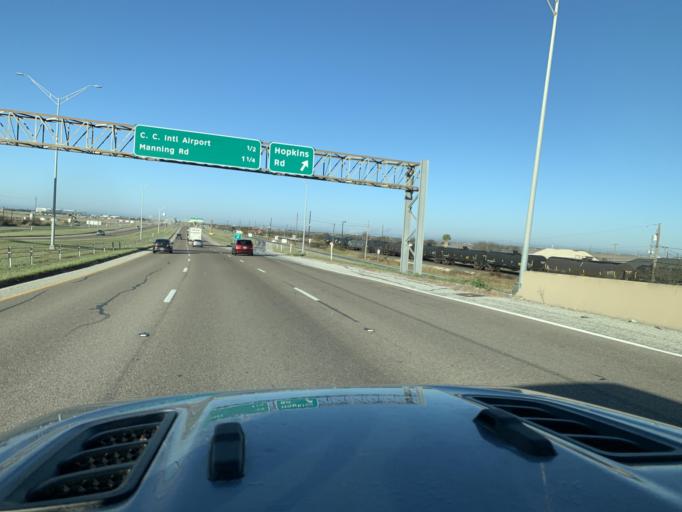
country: US
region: Texas
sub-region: Nueces County
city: Corpus Christi
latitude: 27.7851
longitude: -97.4889
